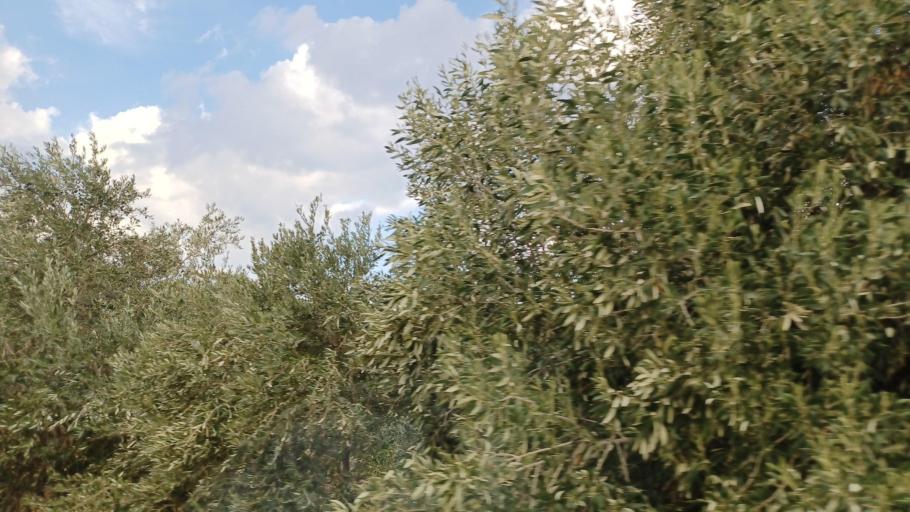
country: CY
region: Pafos
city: Polis
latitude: 35.1047
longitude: 32.5055
